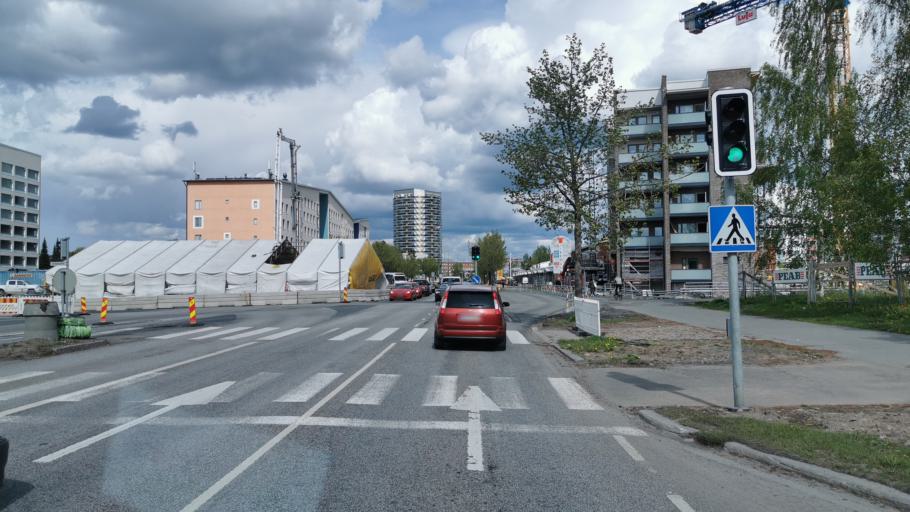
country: FI
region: Northern Ostrobothnia
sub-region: Oulu
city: Oulu
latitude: 65.0002
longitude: 25.4641
